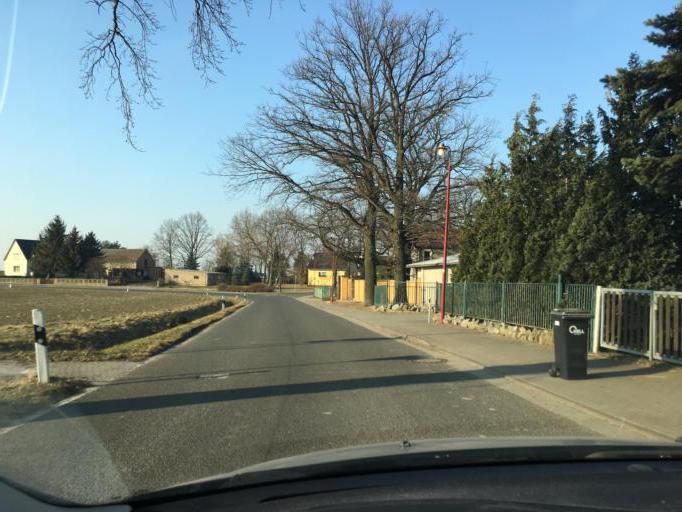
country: DE
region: Saxony
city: Kitzscher
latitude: 51.1862
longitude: 12.5591
